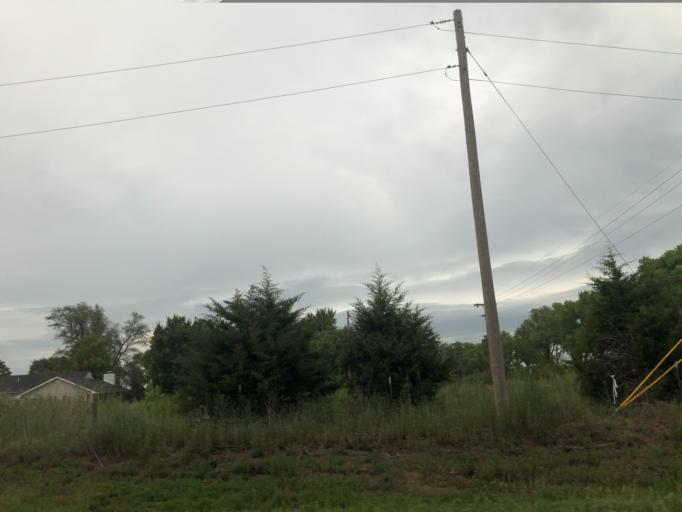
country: US
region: Kansas
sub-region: Reno County
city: Hutchinson
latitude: 38.1148
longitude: -97.9412
